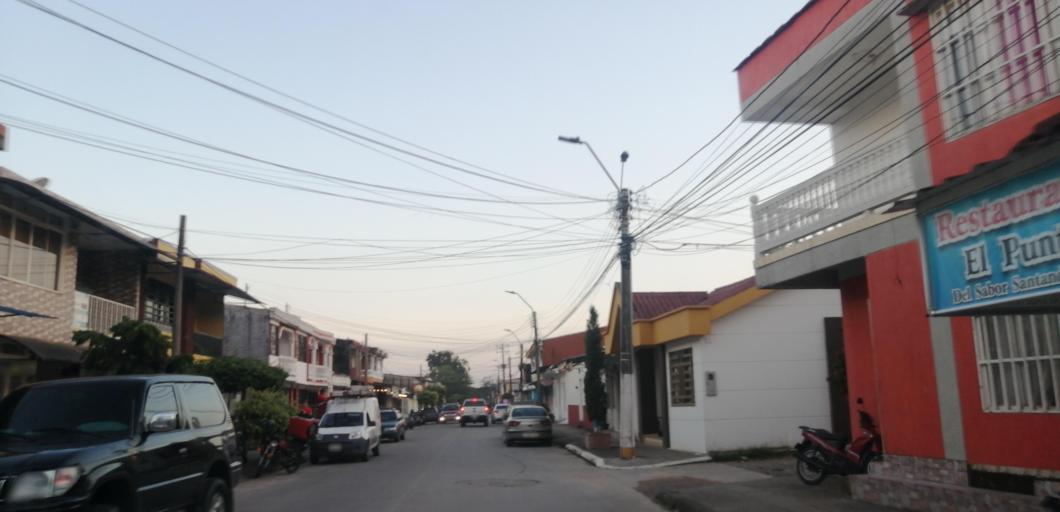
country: CO
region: Meta
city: Acacias
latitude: 3.9972
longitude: -73.7583
